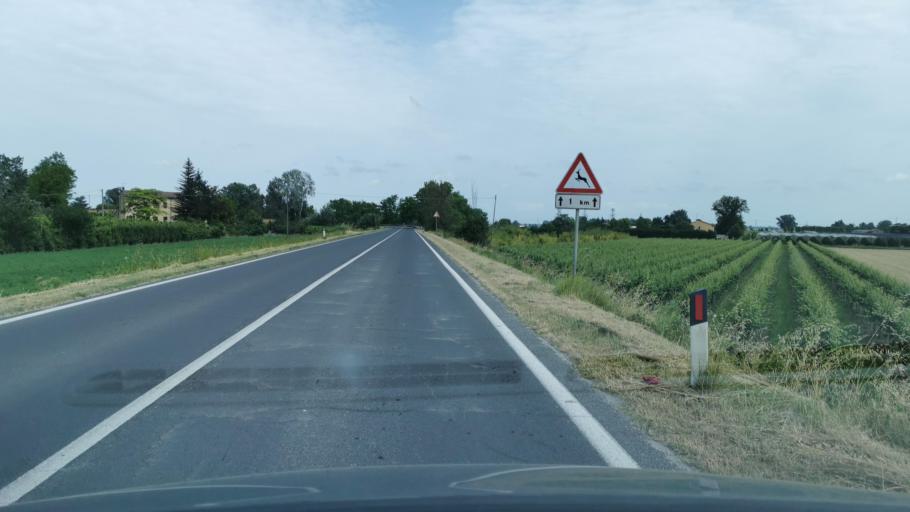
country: IT
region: Emilia-Romagna
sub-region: Provincia di Ravenna
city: Sant'Alberto
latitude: 44.5391
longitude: 12.1348
